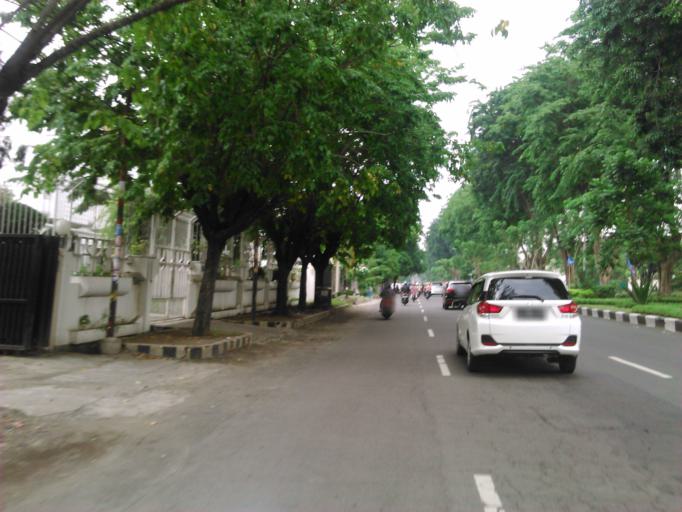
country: ID
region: East Java
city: Mulyorejo
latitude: -7.2807
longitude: 112.7780
